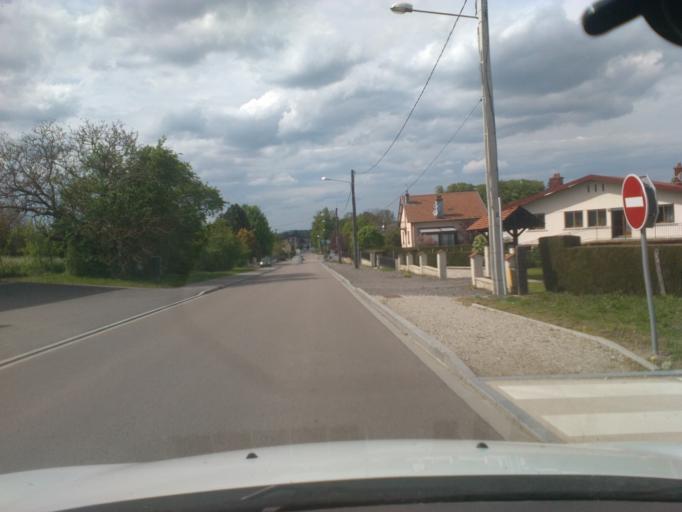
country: FR
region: Lorraine
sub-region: Departement des Vosges
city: Mirecourt
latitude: 48.2685
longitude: 6.1405
